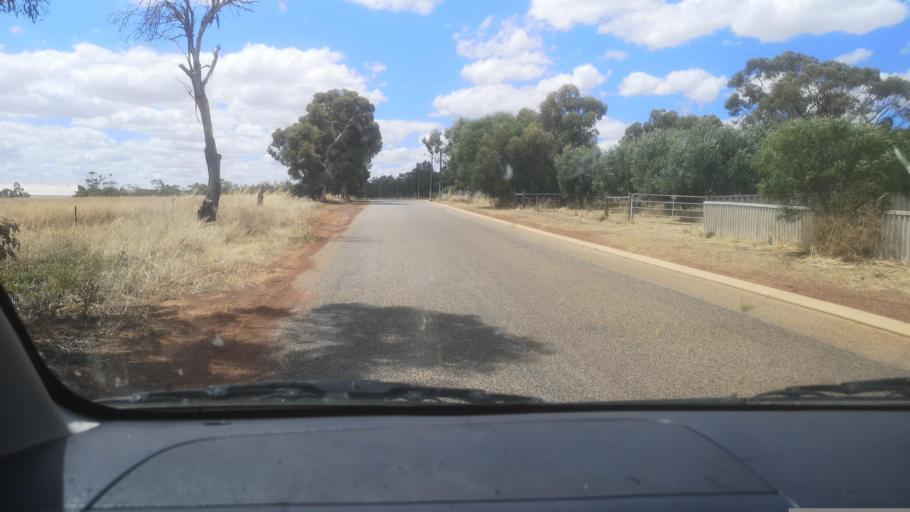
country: AU
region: Western Australia
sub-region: Cunderdin
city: Cunderdin
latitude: -32.0198
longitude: 117.3977
